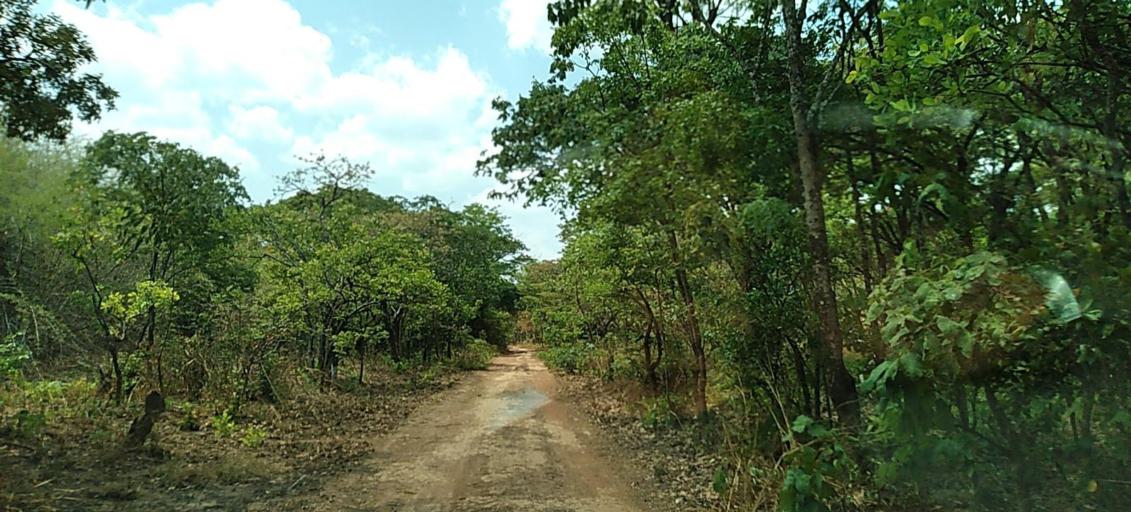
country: ZM
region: Copperbelt
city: Chililabombwe
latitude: -12.4629
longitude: 27.6468
